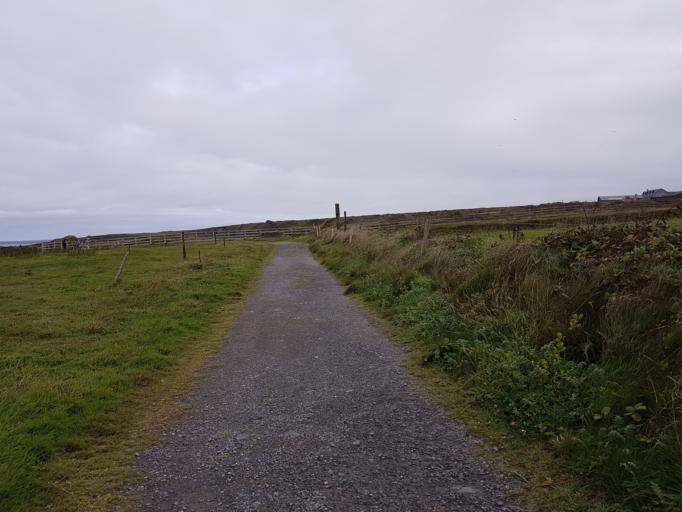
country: IE
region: Munster
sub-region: Ciarrai
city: Ballybunnion
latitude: 52.5165
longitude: -9.6777
